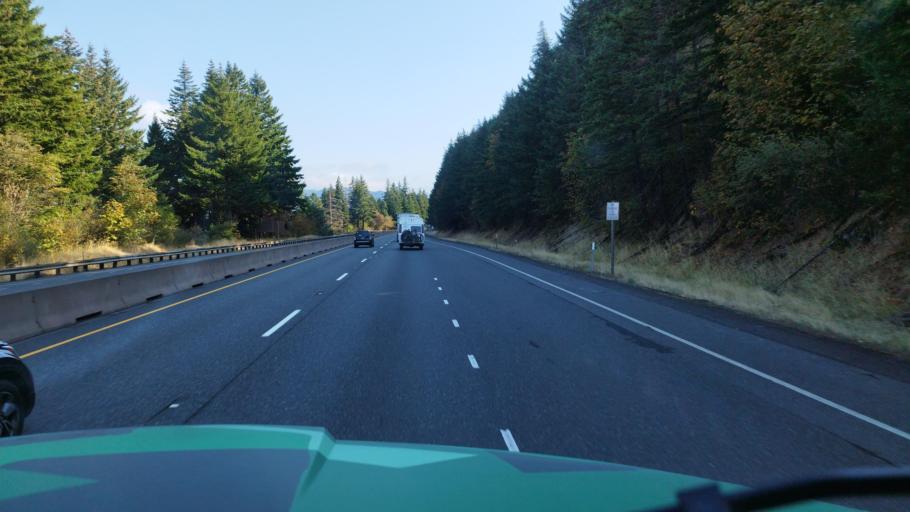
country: US
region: Washington
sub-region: Skamania County
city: Carson
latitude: 45.6924
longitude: -121.8351
